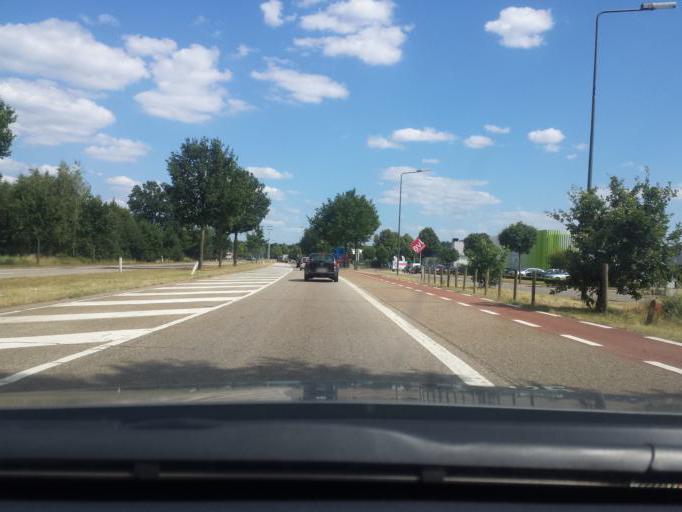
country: BE
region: Flanders
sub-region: Provincie Limburg
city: Beringen
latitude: 51.0389
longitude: 5.2259
